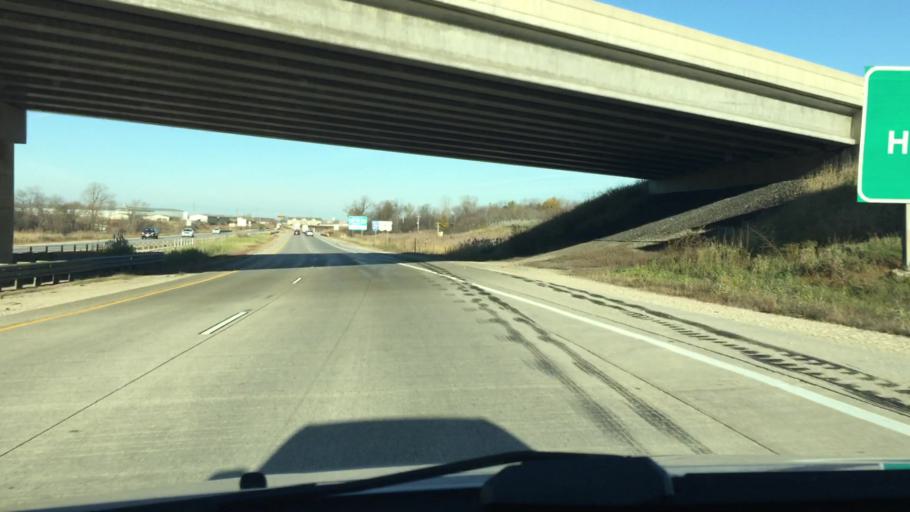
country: US
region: Wisconsin
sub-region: Fond du Lac County
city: Fond du Lac
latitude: 43.7437
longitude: -88.4497
